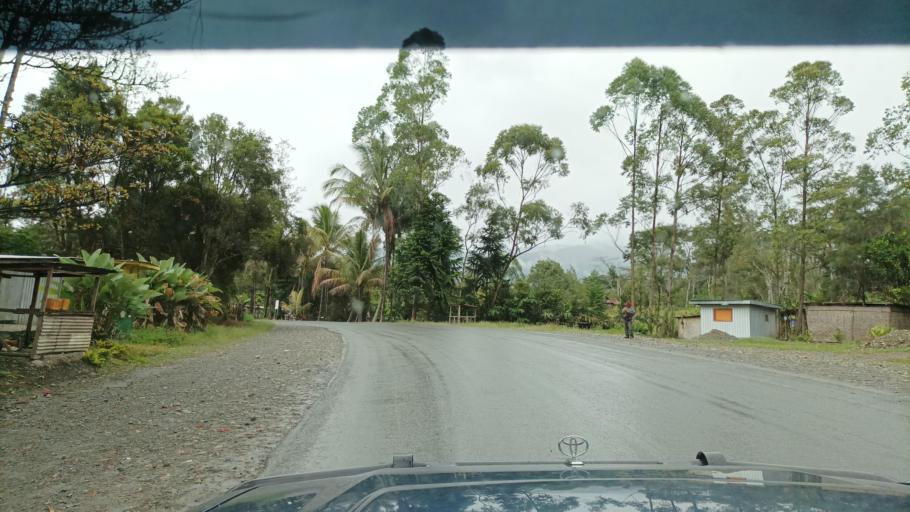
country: PG
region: Jiwaka
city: Minj
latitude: -5.8614
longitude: 144.6378
